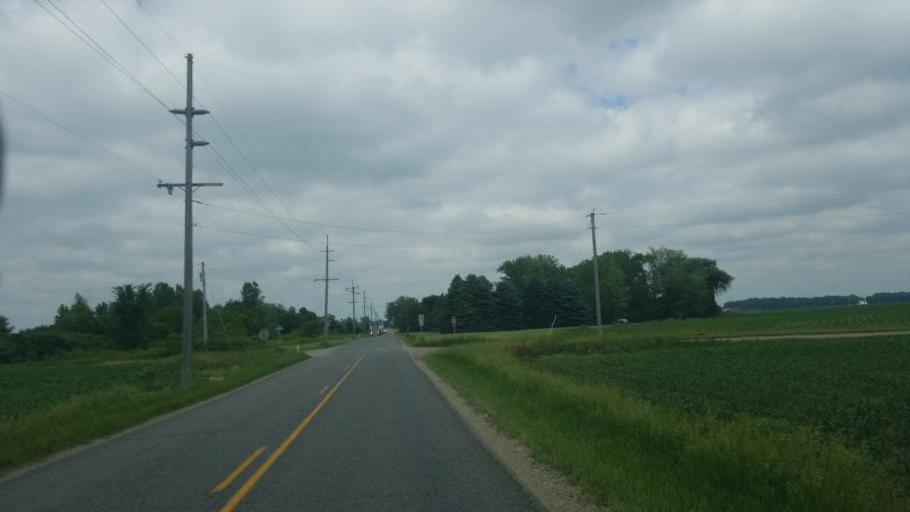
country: US
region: Indiana
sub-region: Elkhart County
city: Wakarusa
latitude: 41.4838
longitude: -86.0408
